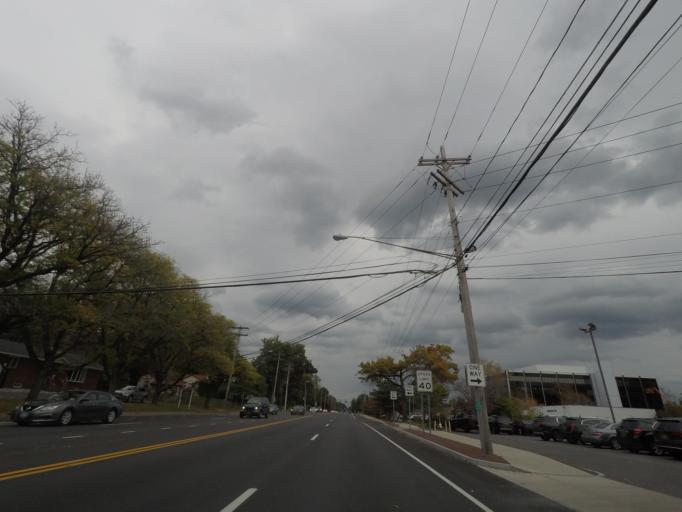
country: US
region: New York
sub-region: Albany County
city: McKownville
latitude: 42.6814
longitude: -73.8385
